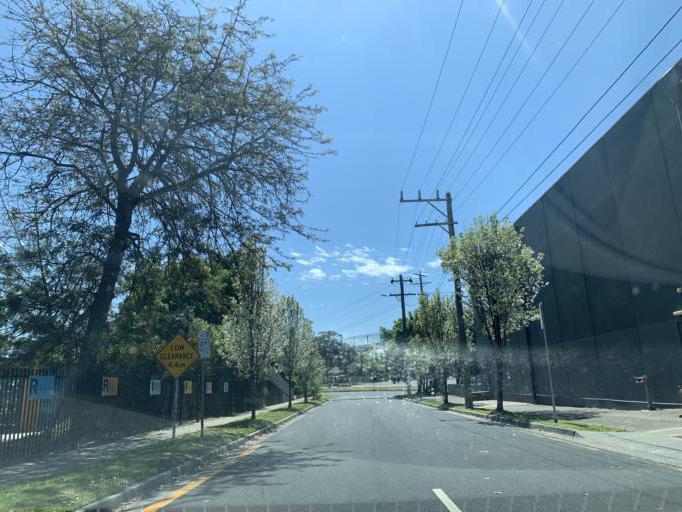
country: AU
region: Victoria
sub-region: Bayside
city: Moorabbin
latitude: -37.9419
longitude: 145.0399
